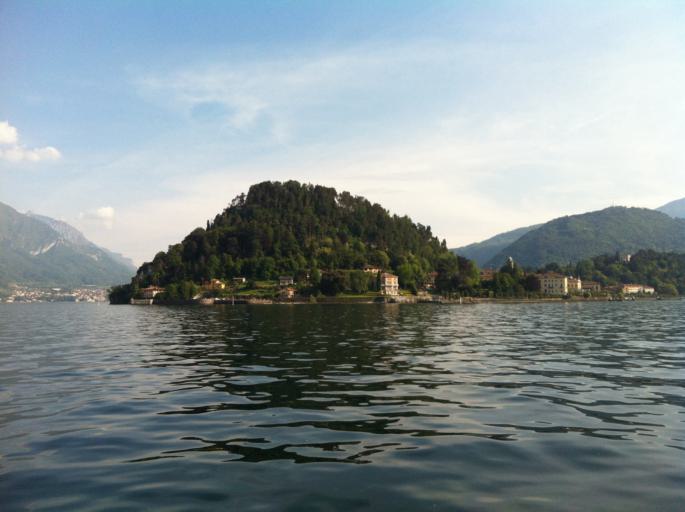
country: IT
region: Lombardy
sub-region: Provincia di Como
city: Bellagio
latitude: 45.9954
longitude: 9.2613
